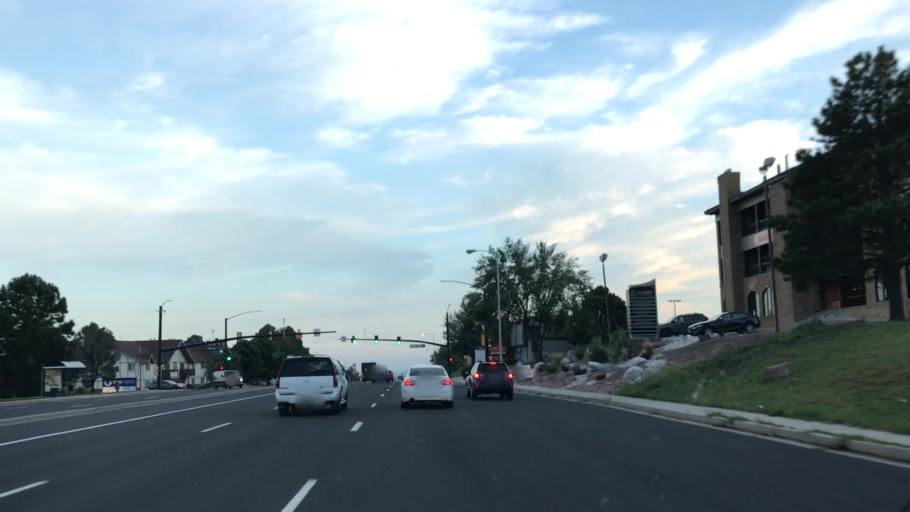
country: US
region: Colorado
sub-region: El Paso County
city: Cimarron Hills
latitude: 38.8779
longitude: -104.7572
